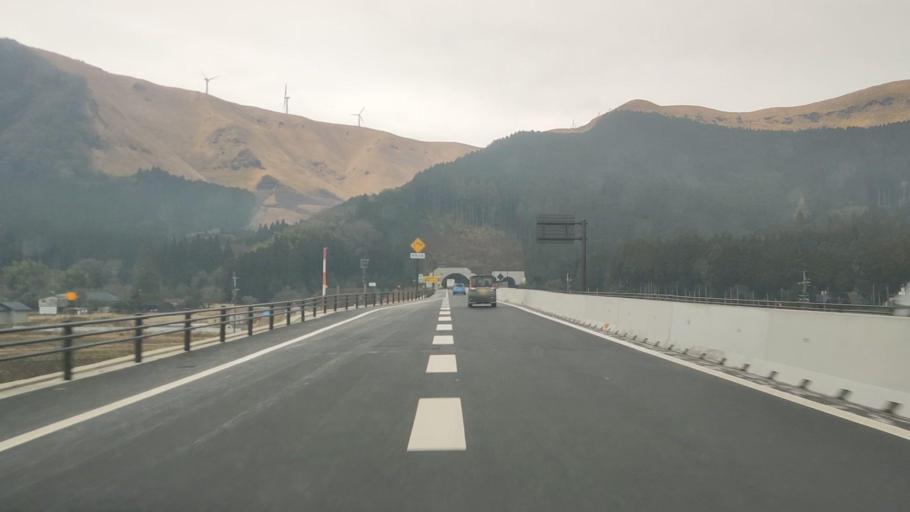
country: JP
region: Kumamoto
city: Aso
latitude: 32.9144
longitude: 130.9791
